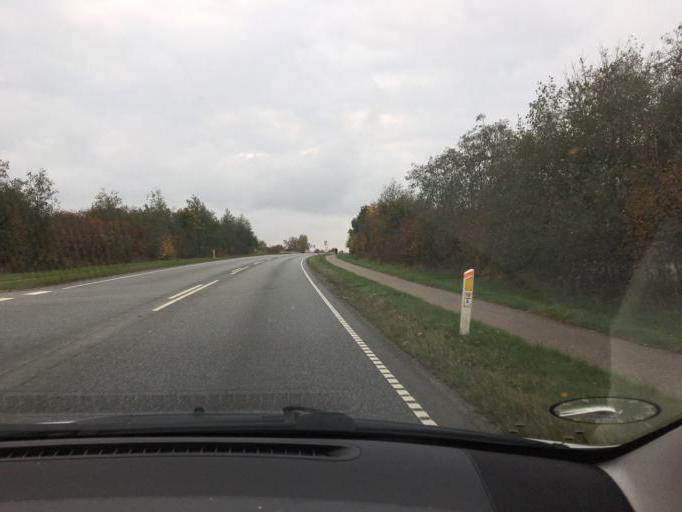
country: DK
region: South Denmark
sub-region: Fredericia Kommune
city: Fredericia
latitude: 55.6043
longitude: 9.7582
